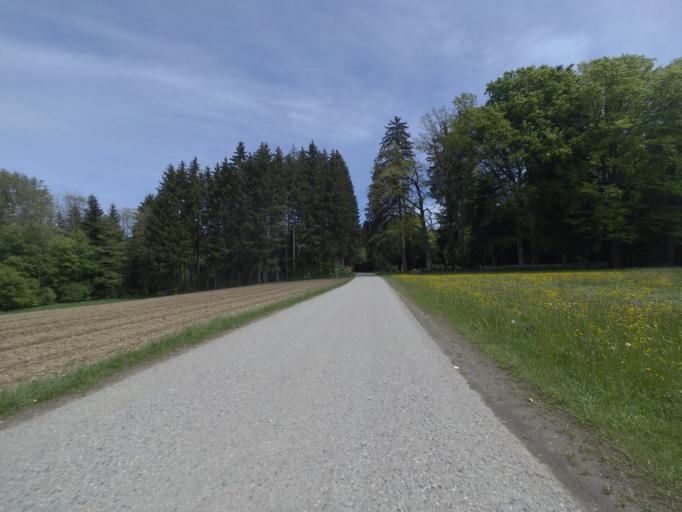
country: AT
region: Salzburg
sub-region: Politischer Bezirk Salzburg-Umgebung
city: Mattsee
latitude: 48.0039
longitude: 13.1046
